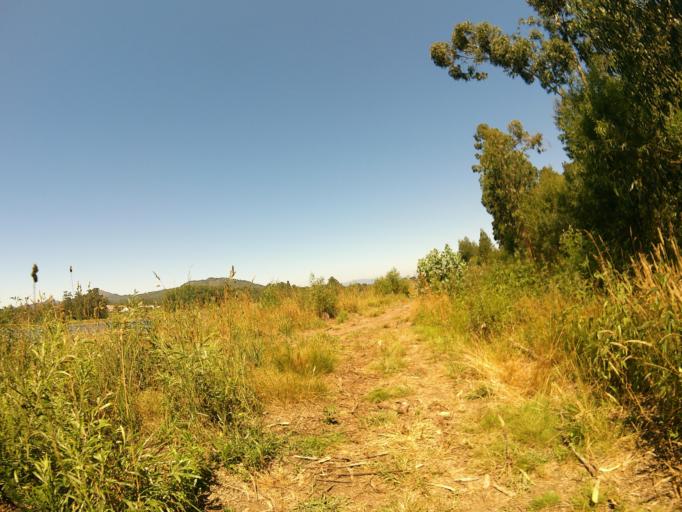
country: PT
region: Viana do Castelo
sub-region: Viana do Castelo
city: Darque
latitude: 41.6949
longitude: -8.7650
